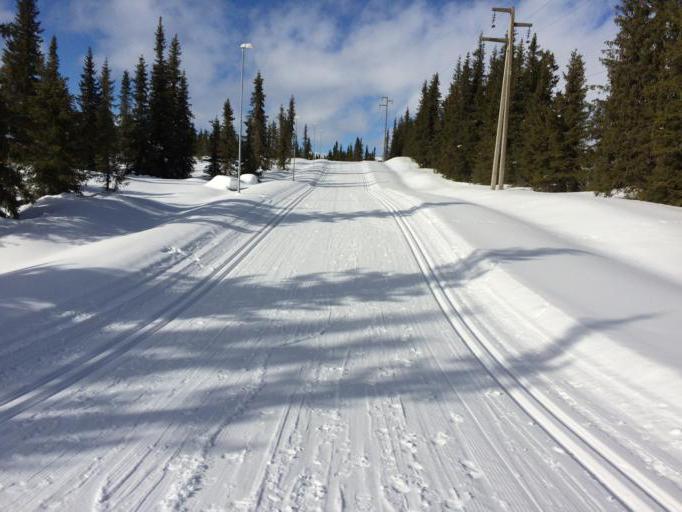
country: NO
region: Oppland
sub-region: Gausdal
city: Segalstad bru
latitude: 61.3296
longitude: 10.0942
